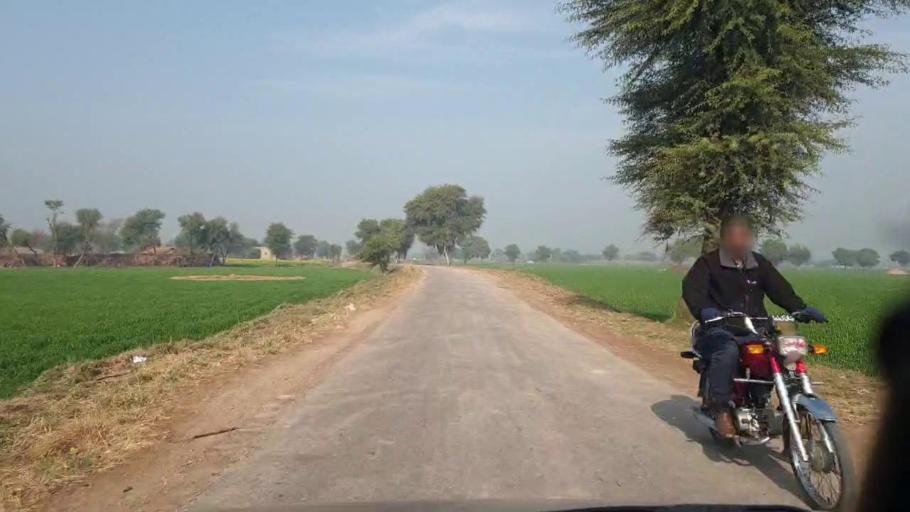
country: PK
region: Sindh
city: Shahdadpur
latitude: 26.0063
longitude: 68.5511
